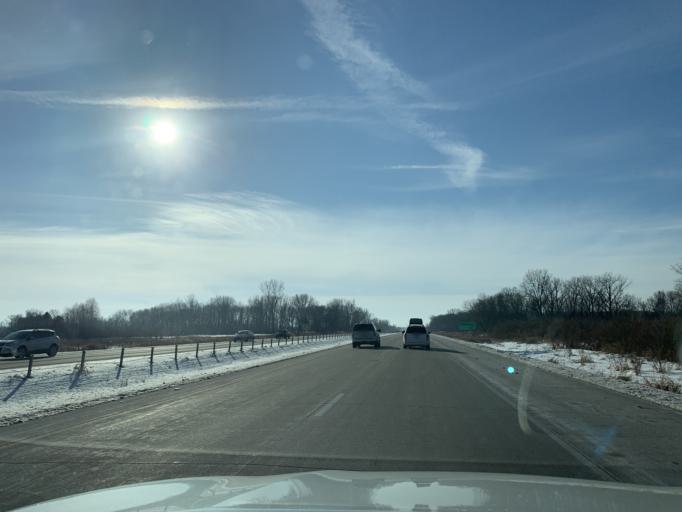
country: US
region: Minnesota
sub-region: Anoka County
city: Centerville
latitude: 45.2105
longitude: -93.0401
